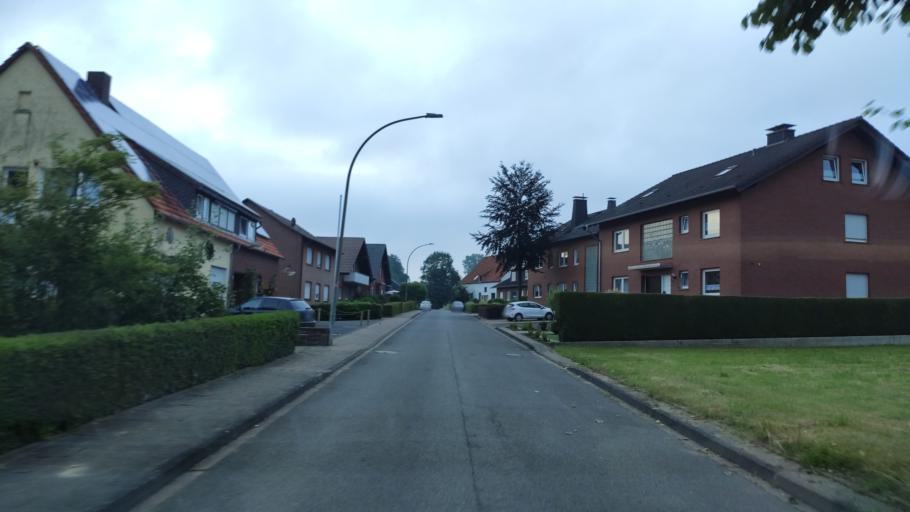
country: DE
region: North Rhine-Westphalia
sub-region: Regierungsbezirk Detmold
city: Schieder-Schwalenberg
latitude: 51.8083
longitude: 9.1896
